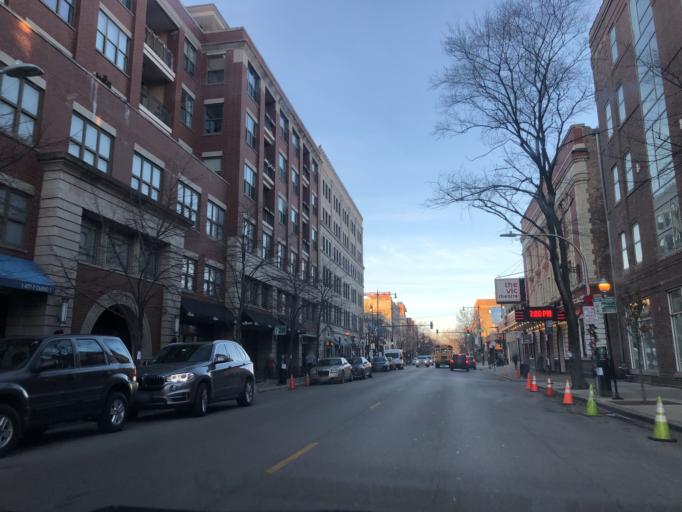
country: US
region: Illinois
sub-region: Cook County
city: Chicago
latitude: 41.9389
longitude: -87.6541
